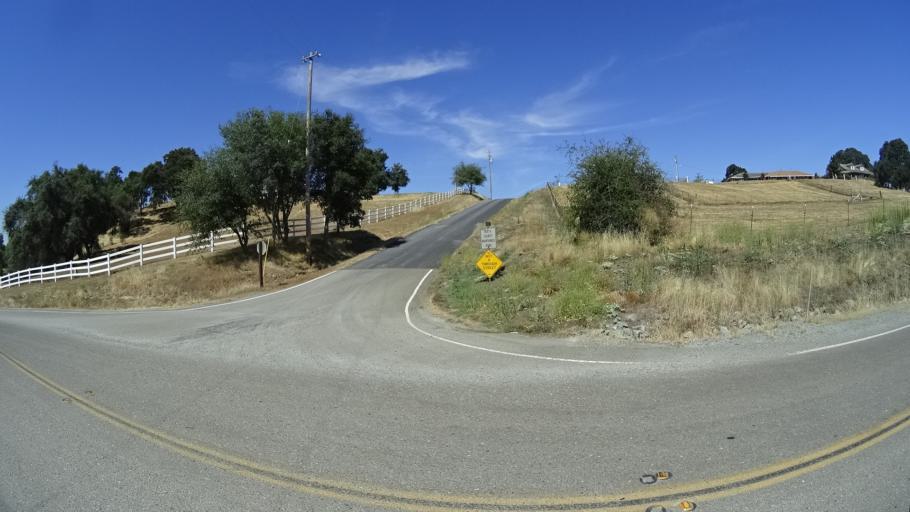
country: US
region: California
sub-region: Calaveras County
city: Rancho Calaveras
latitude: 38.1140
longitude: -120.9086
